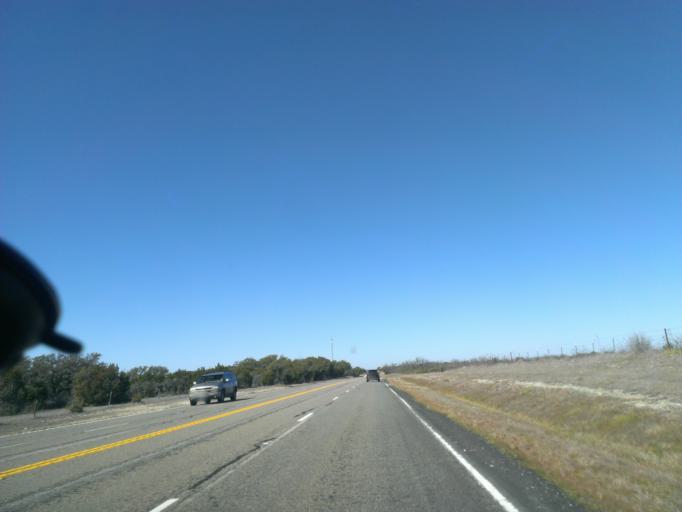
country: US
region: Texas
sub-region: Lampasas County
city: Kempner
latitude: 30.9139
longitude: -97.9767
